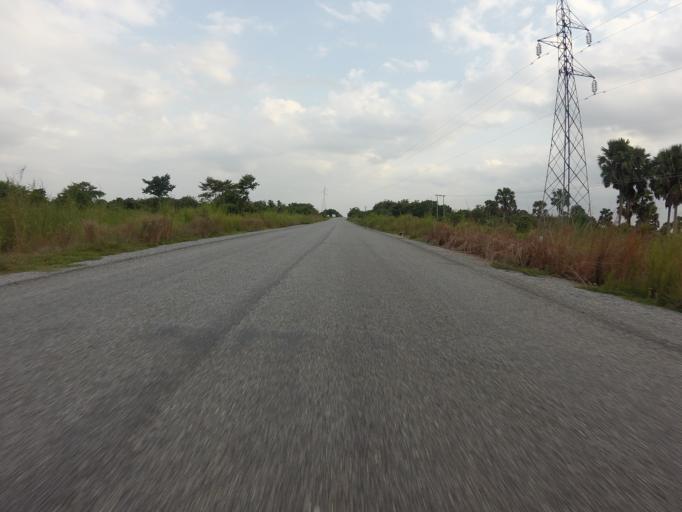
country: GH
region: Volta
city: Ho
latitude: 6.3971
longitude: 0.5257
